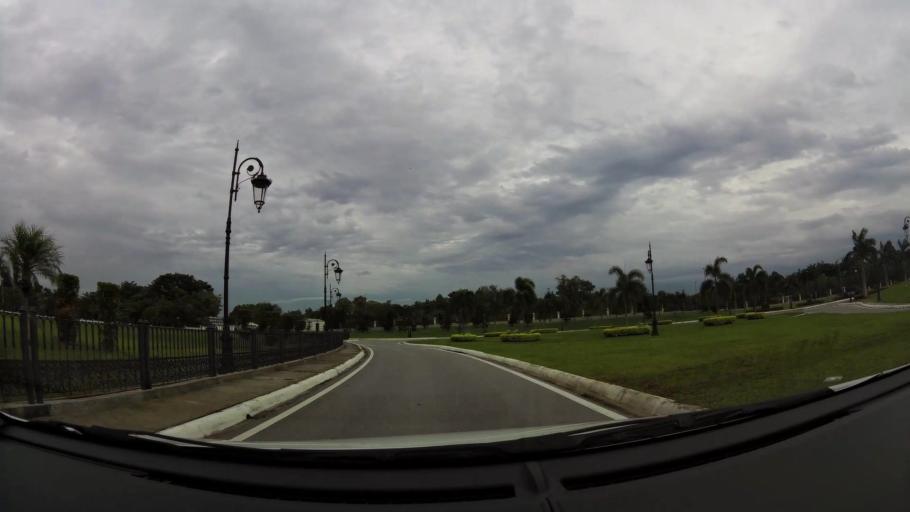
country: BN
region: Brunei and Muara
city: Bandar Seri Begawan
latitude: 4.9191
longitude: 114.9357
